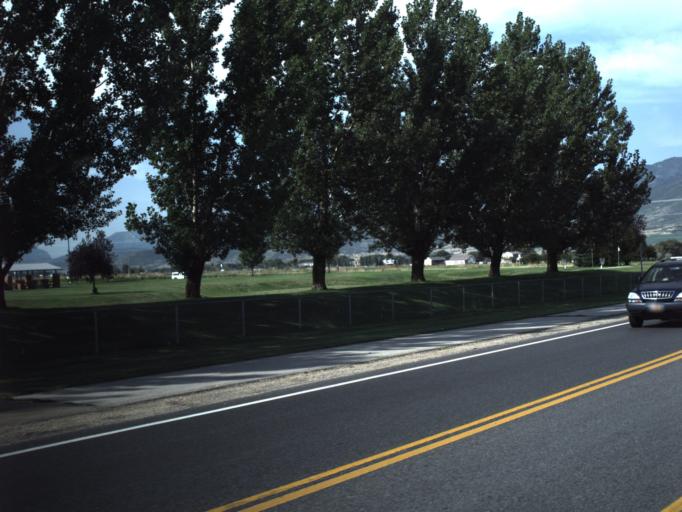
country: US
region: Utah
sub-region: Wasatch County
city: Heber
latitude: 40.5069
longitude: -111.4317
